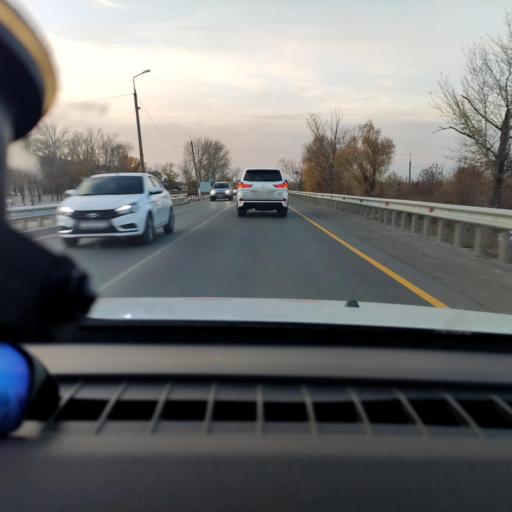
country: RU
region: Samara
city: Samara
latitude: 53.1159
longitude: 50.1245
